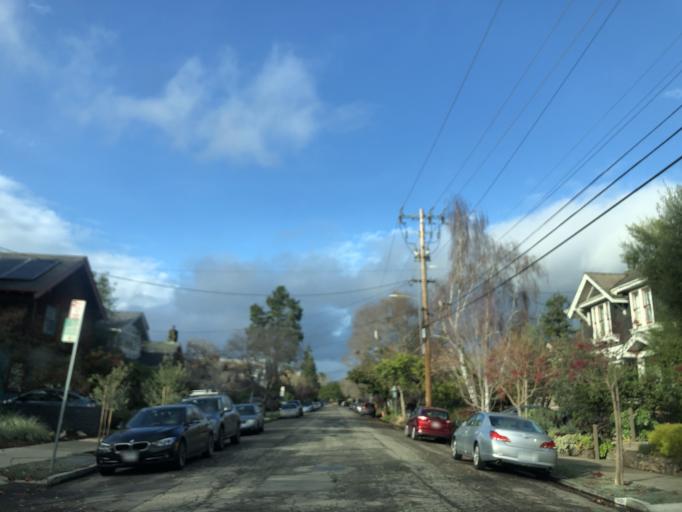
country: US
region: California
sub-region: Alameda County
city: Berkeley
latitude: 37.8518
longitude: -122.2559
